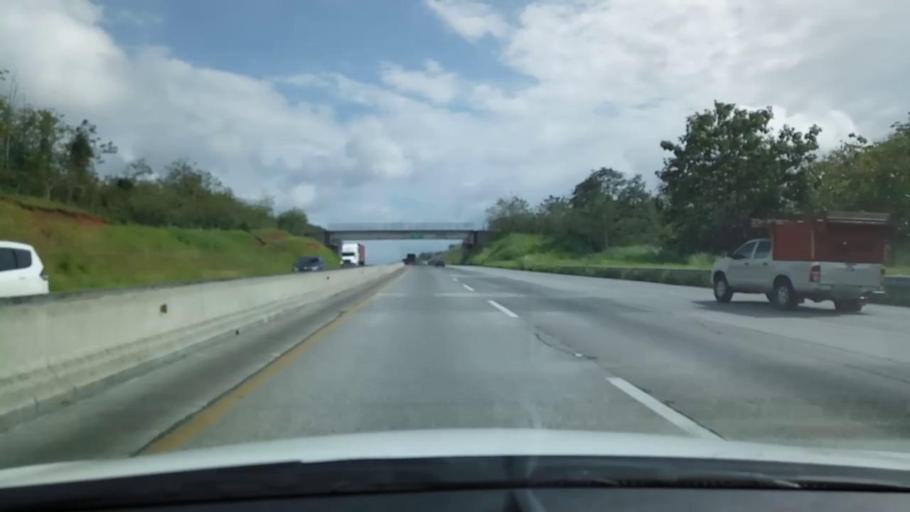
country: PA
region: Colon
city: El Giral
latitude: 9.2478
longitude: -79.6874
